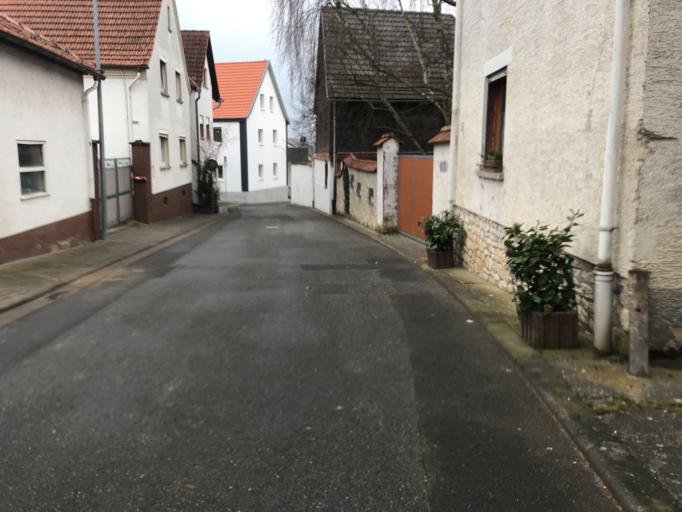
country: DE
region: Rheinland-Pfalz
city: Essenheim
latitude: 49.9321
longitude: 8.1605
